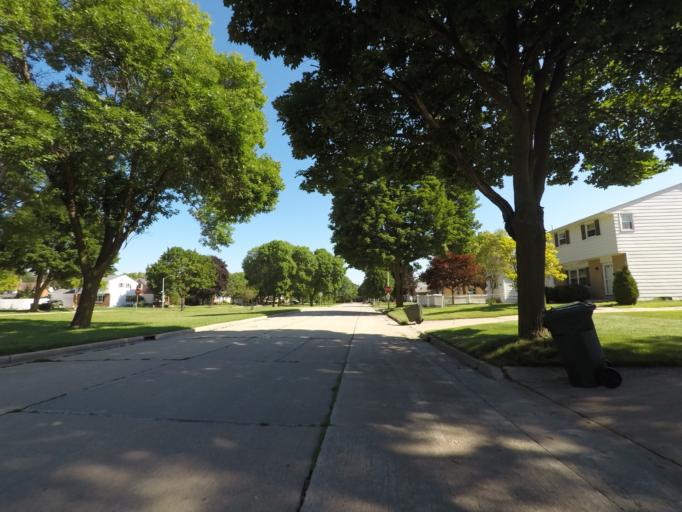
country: US
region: Wisconsin
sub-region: Waukesha County
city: Elm Grove
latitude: 43.0214
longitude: -88.0619
